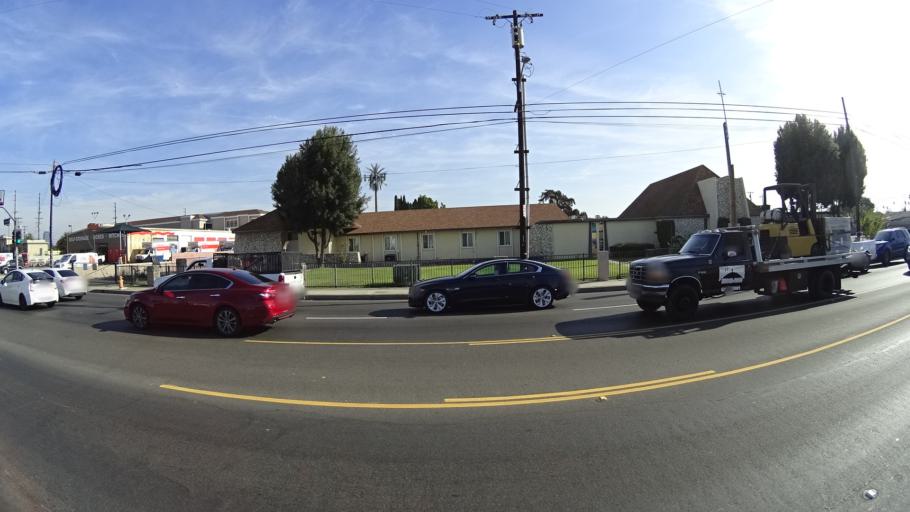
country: US
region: California
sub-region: Orange County
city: Garden Grove
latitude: 33.7733
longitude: -117.9031
